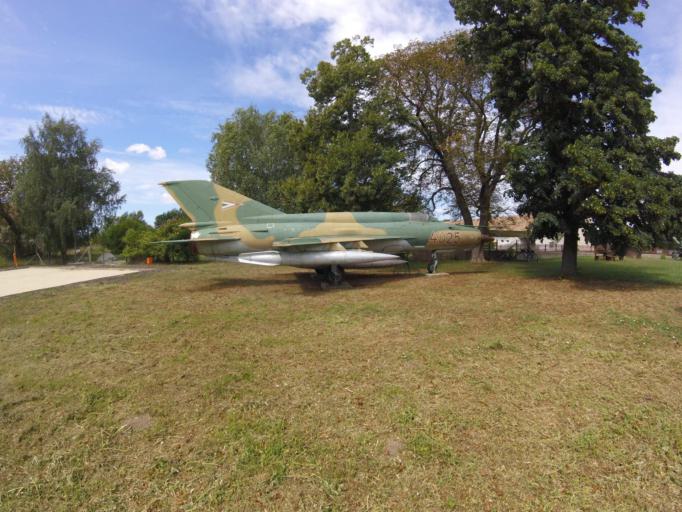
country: HU
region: Gyor-Moson-Sopron
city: Szany
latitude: 47.3771
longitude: 17.2858
